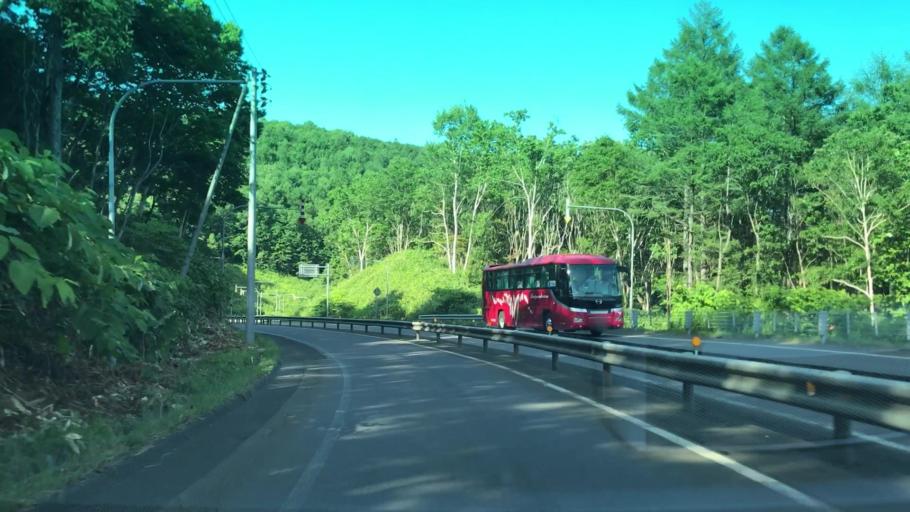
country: JP
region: Hokkaido
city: Yoichi
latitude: 43.0627
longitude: 140.6935
